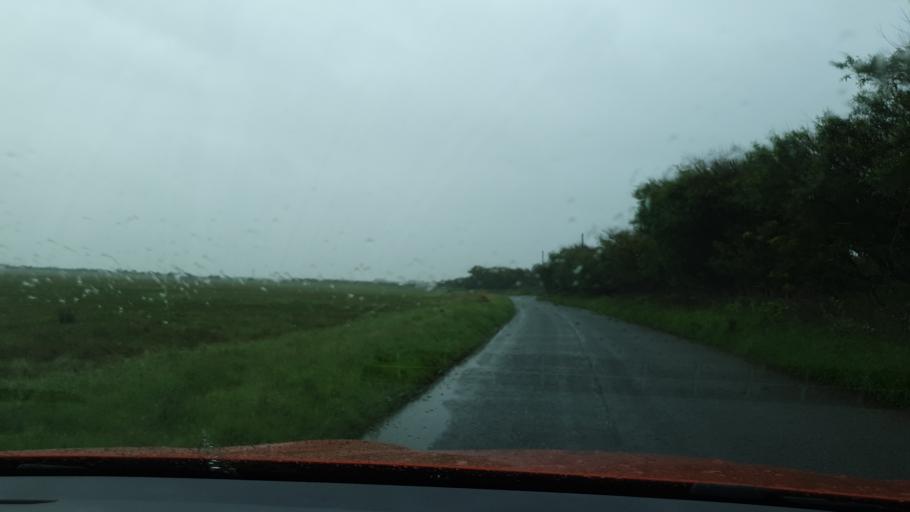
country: GB
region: England
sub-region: Cumbria
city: Barrow in Furness
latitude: 54.0668
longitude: -3.2246
